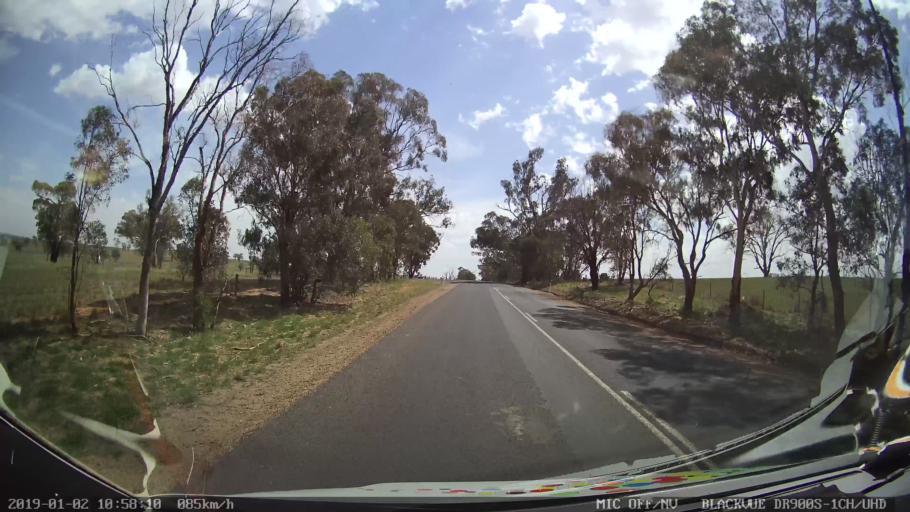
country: AU
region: New South Wales
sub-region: Cootamundra
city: Cootamundra
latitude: -34.6273
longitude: 148.2889
